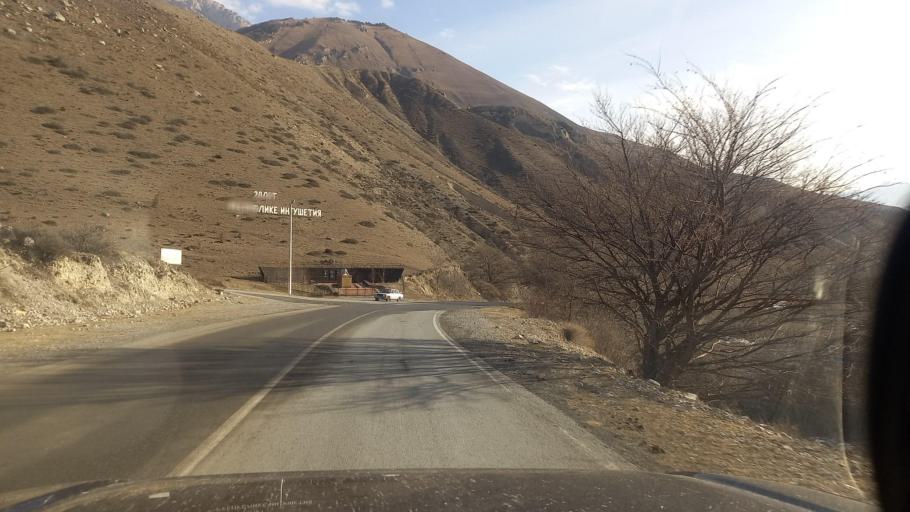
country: RU
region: Ingushetiya
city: Dzhayrakh
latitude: 42.8429
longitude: 44.6521
